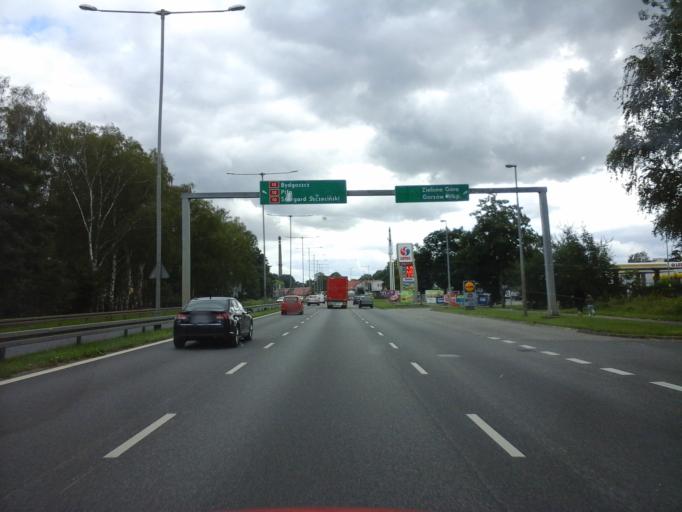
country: PL
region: West Pomeranian Voivodeship
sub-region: Powiat gryfinski
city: Stare Czarnowo
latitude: 53.3626
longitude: 14.7401
